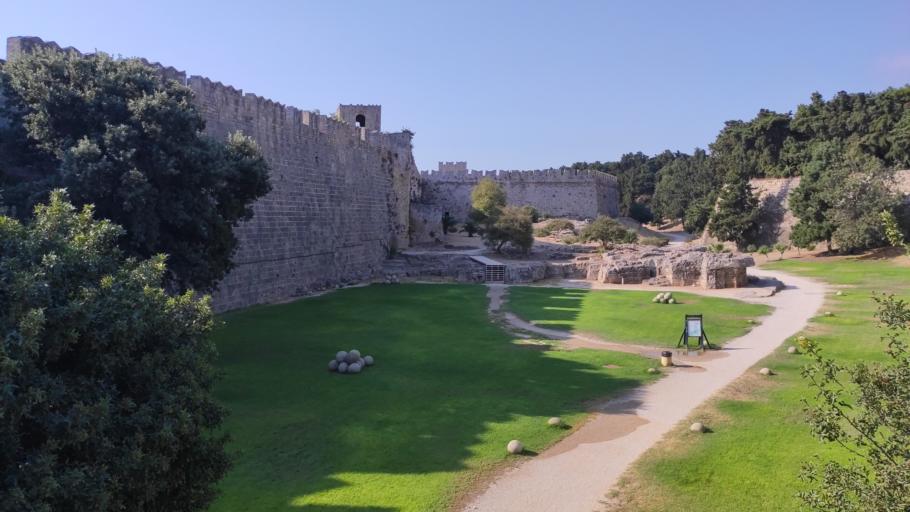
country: GR
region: South Aegean
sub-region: Nomos Dodekanisou
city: Rodos
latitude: 36.4460
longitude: 28.2224
